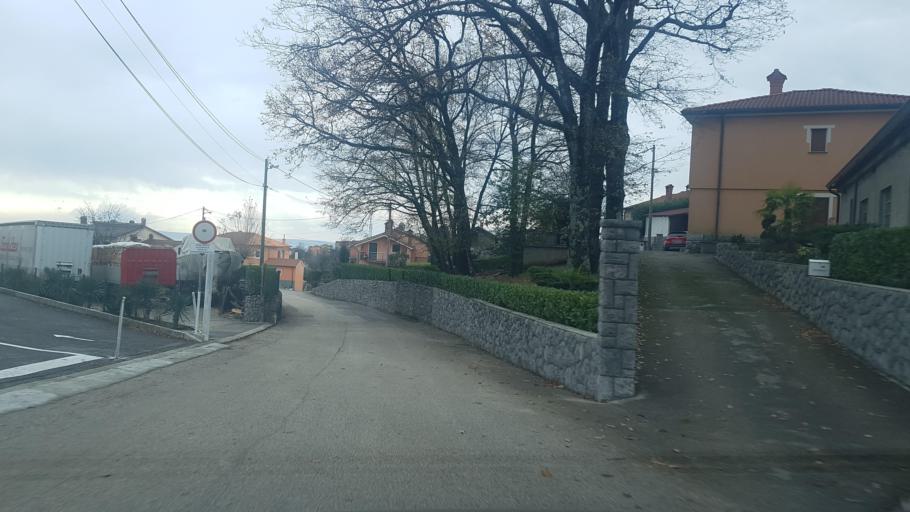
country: HR
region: Primorsko-Goranska
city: Matulji
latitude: 45.3774
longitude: 14.3177
